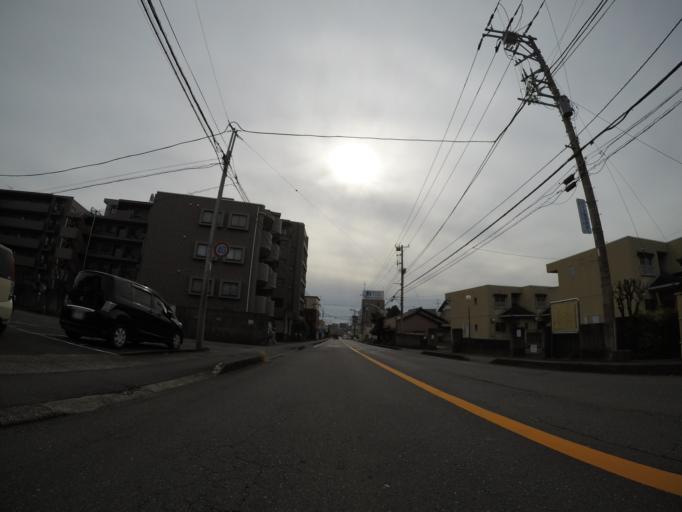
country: JP
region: Shizuoka
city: Fuji
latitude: 35.1730
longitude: 138.6817
